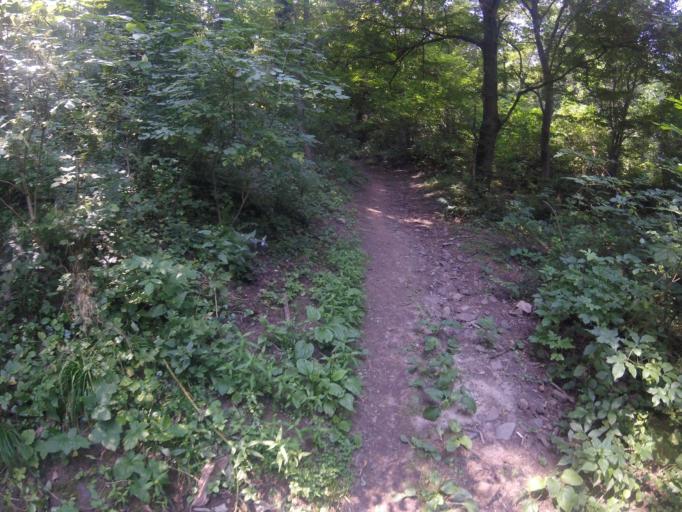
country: HU
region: Veszprem
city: Badacsonytomaj
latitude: 46.8077
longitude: 17.4958
